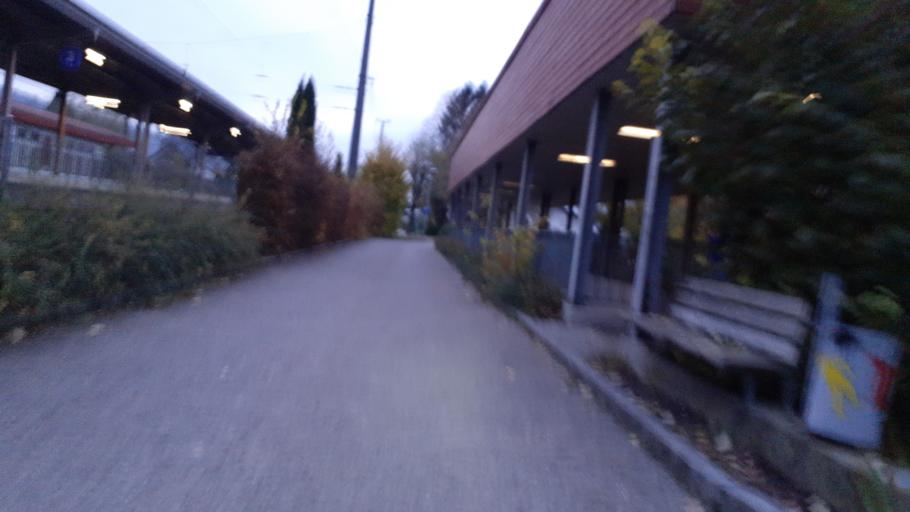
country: AT
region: Vorarlberg
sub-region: Politischer Bezirk Feldkirch
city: Gotzis
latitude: 47.3370
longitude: 9.6366
